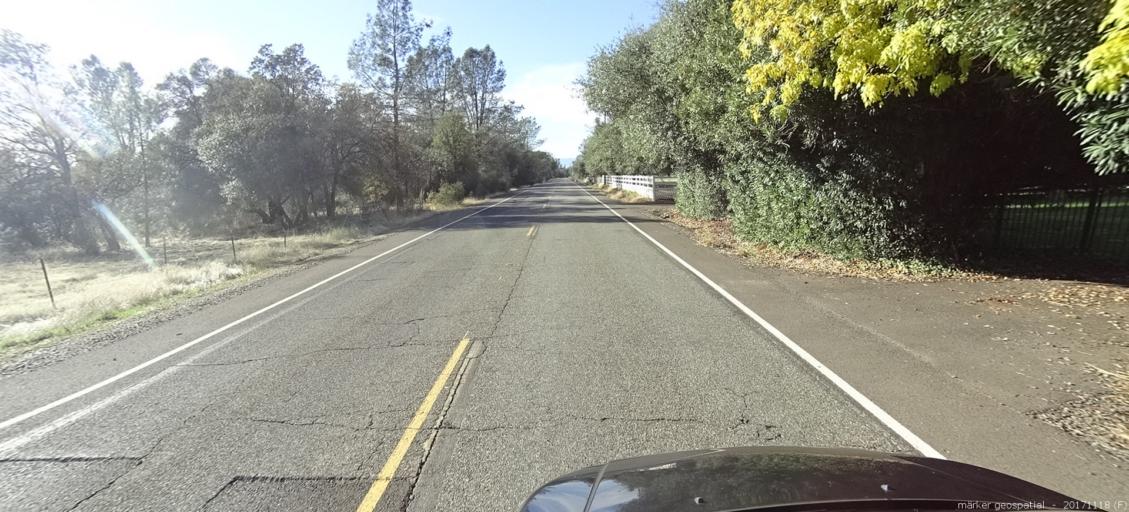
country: US
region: California
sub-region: Shasta County
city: Redding
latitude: 40.4780
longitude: -122.4168
